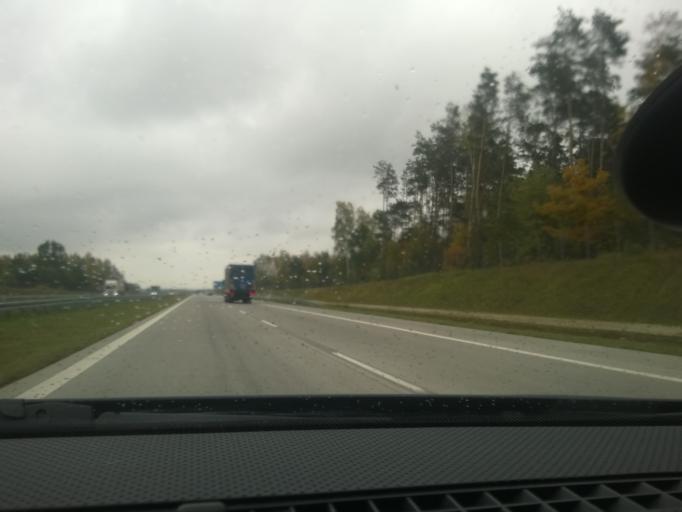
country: PL
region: Lodz Voivodeship
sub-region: Powiat lodzki wschodni
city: Brojce
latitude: 51.6664
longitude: 19.5854
